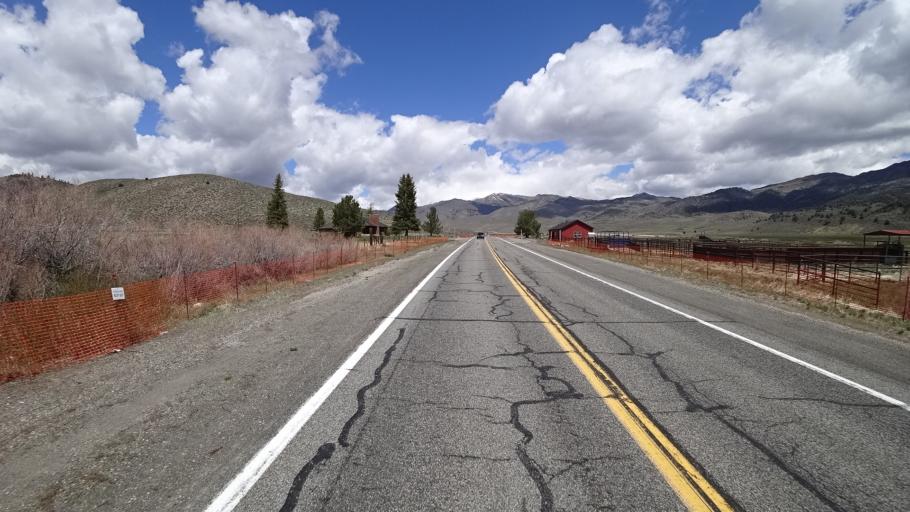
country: US
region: California
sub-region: Mono County
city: Bridgeport
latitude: 38.3076
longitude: -119.3143
